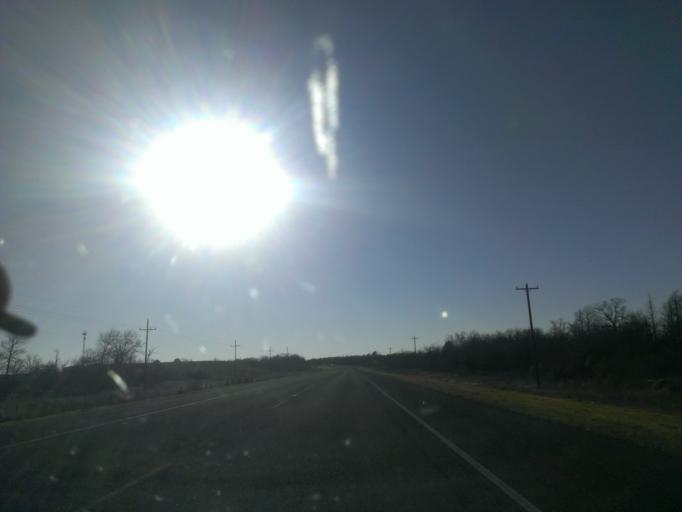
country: US
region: Texas
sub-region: Bastrop County
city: Elgin
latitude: 30.3777
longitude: -97.2515
